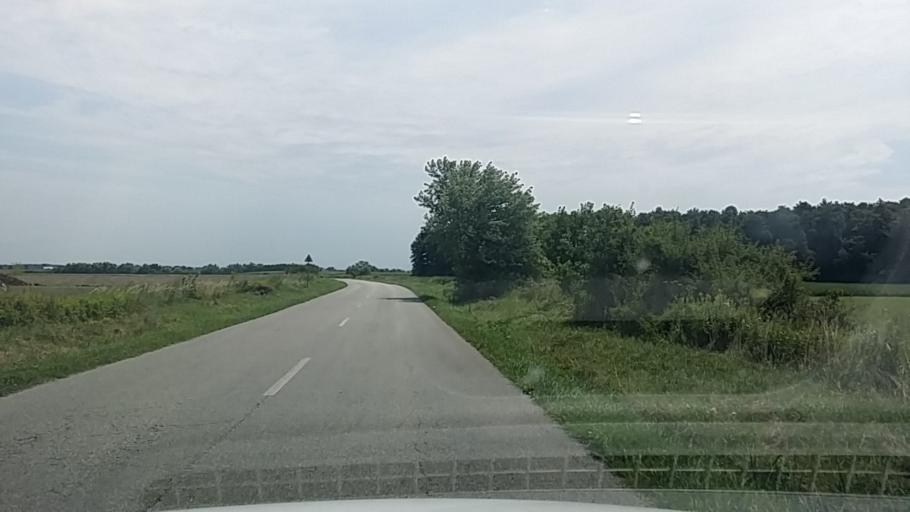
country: HU
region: Zala
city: Becsehely
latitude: 46.4099
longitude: 16.7785
